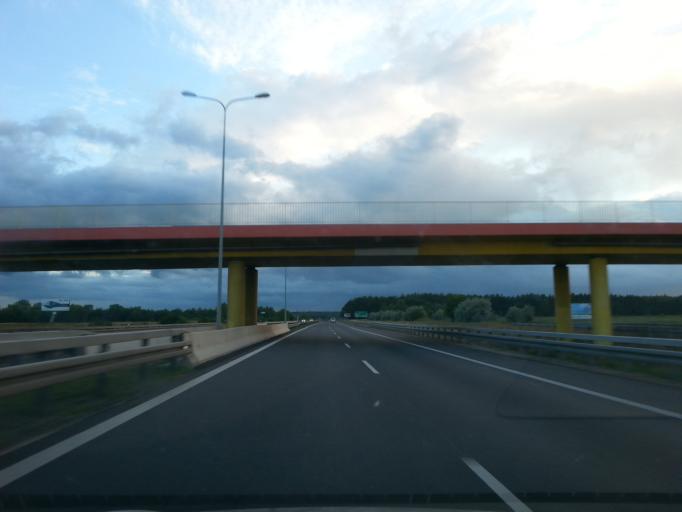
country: PL
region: Lower Silesian Voivodeship
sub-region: Powiat olesnicki
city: Olesnica
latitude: 51.2291
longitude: 17.4686
